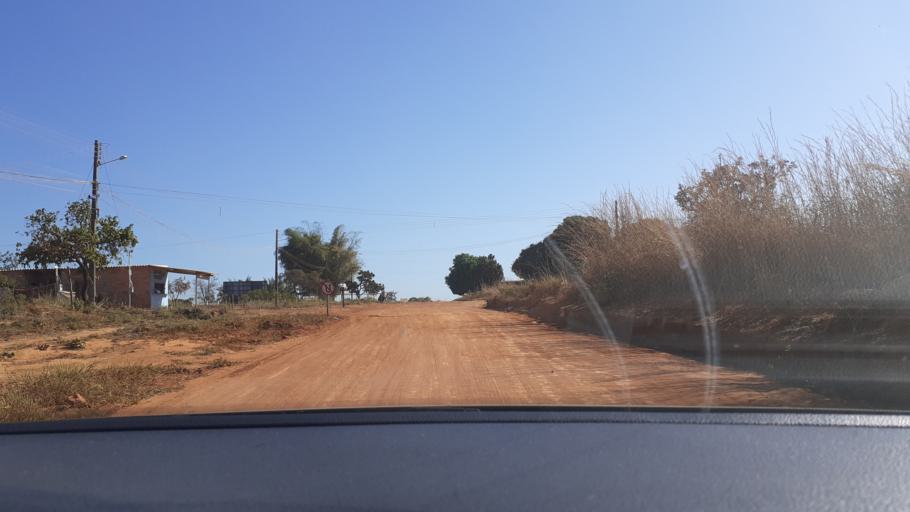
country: BR
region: Goias
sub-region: Aparecida De Goiania
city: Aparecida de Goiania
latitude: -16.8667
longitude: -49.2559
